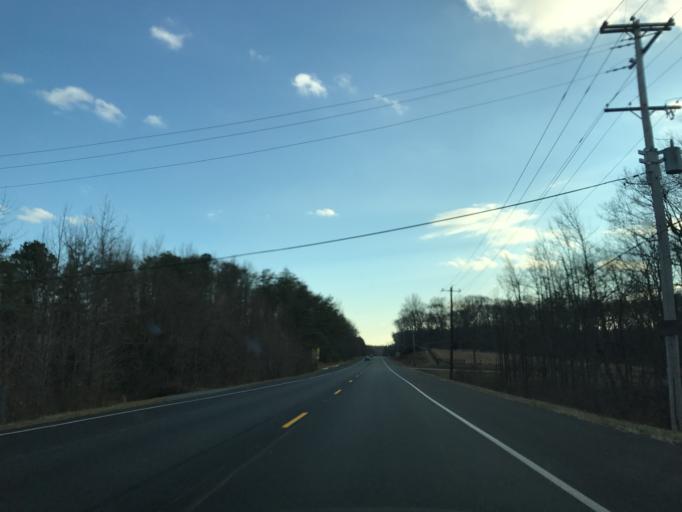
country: US
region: Maryland
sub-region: Cecil County
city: North East
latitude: 39.5858
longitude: -75.9426
